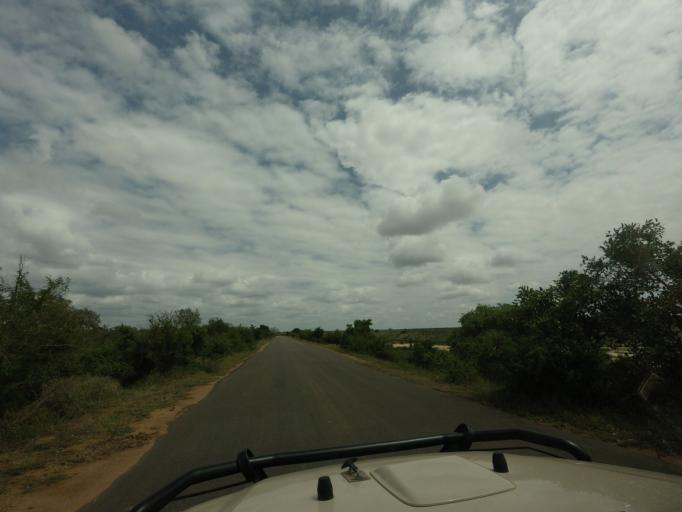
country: ZA
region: Mpumalanga
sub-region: Ehlanzeni District
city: Komatipoort
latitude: -25.1083
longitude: 31.9044
